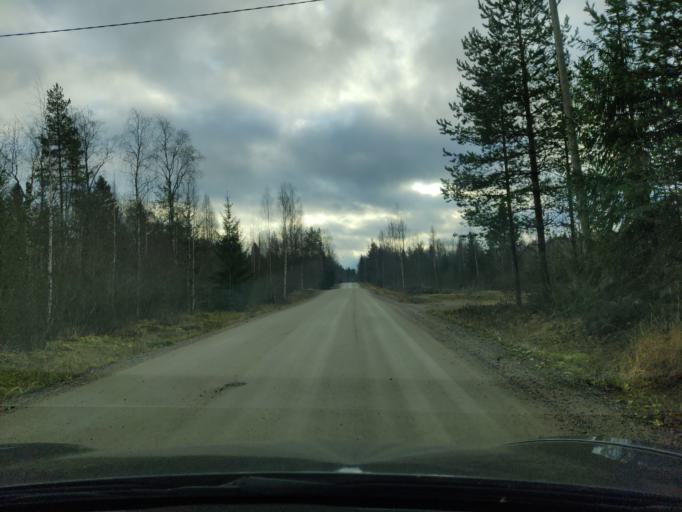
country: FI
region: Northern Savo
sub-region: Ylae-Savo
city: Kiuruvesi
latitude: 63.6407
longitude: 26.6322
